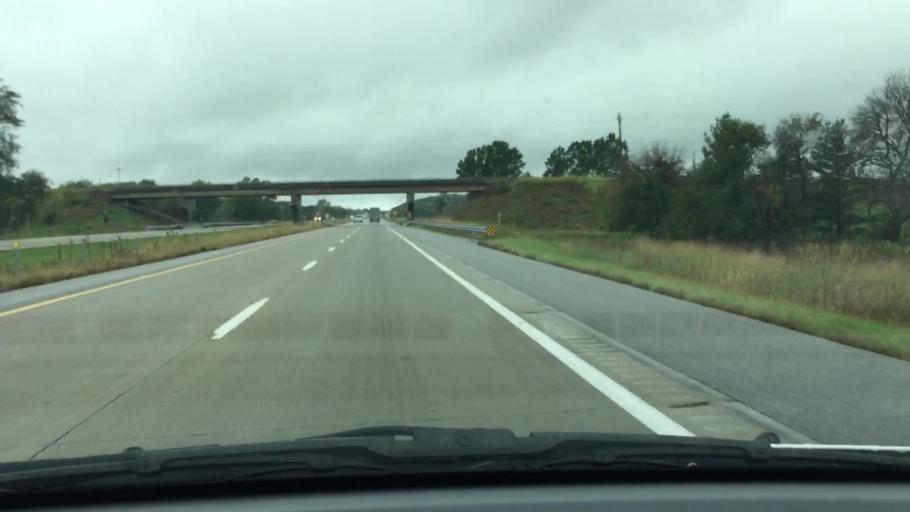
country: US
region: Iowa
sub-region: Jasper County
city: Colfax
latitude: 41.6925
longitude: -93.2452
